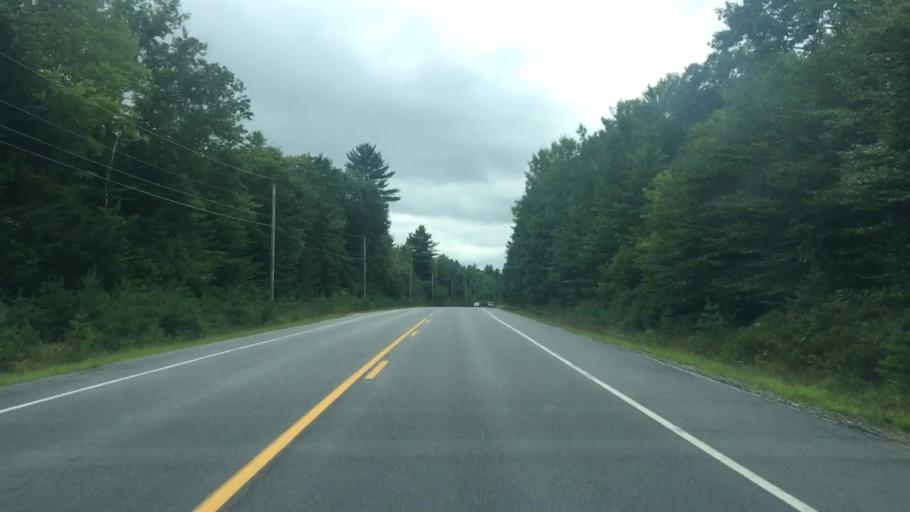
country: US
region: Maine
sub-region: York County
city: Limerick
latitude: 43.7454
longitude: -70.8134
